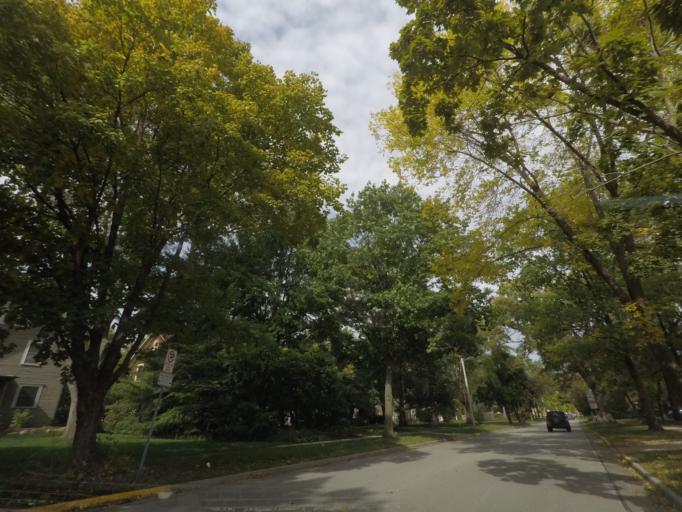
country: US
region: Iowa
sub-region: Story County
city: Ames
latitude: 42.0176
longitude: -93.6443
